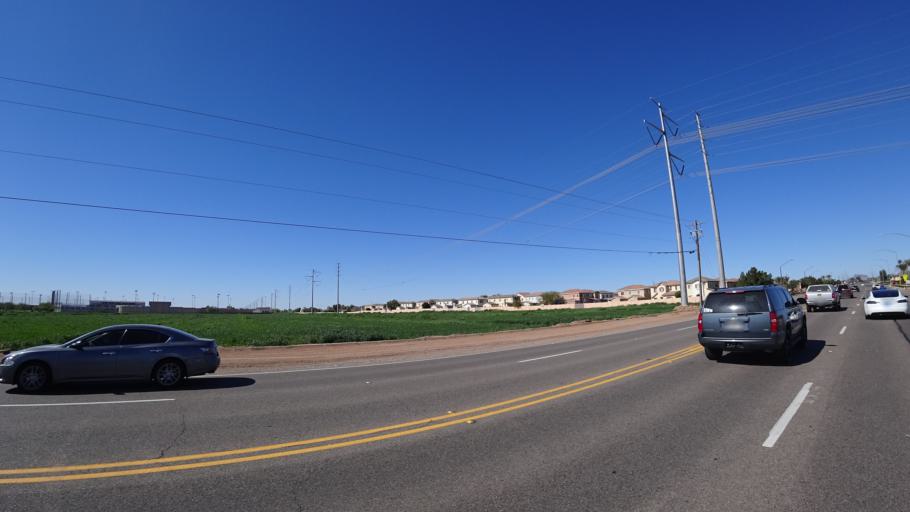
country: US
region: Arizona
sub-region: Maricopa County
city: Gilbert
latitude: 33.3566
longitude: -111.6874
